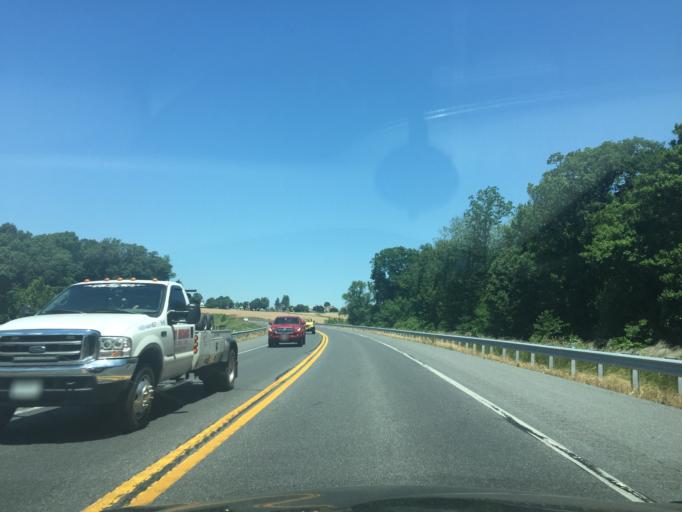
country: US
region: Maryland
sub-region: Carroll County
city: Hampstead
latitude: 39.5907
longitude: -76.8538
